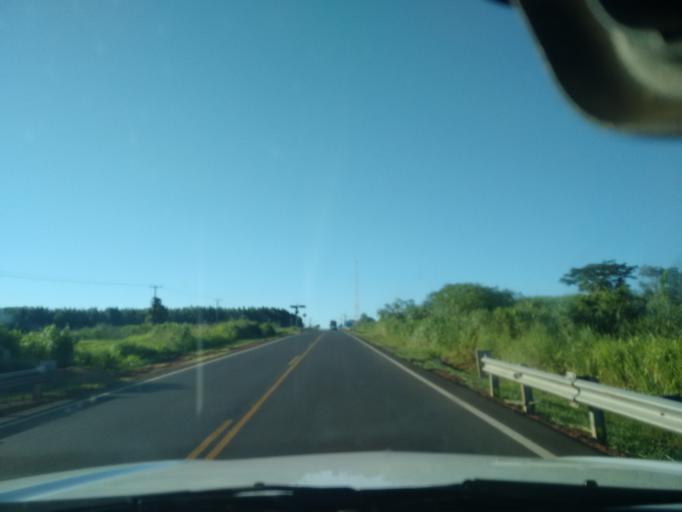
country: BR
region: Mato Grosso do Sul
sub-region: Eldorado
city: Eldorado
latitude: -23.8725
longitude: -54.3248
